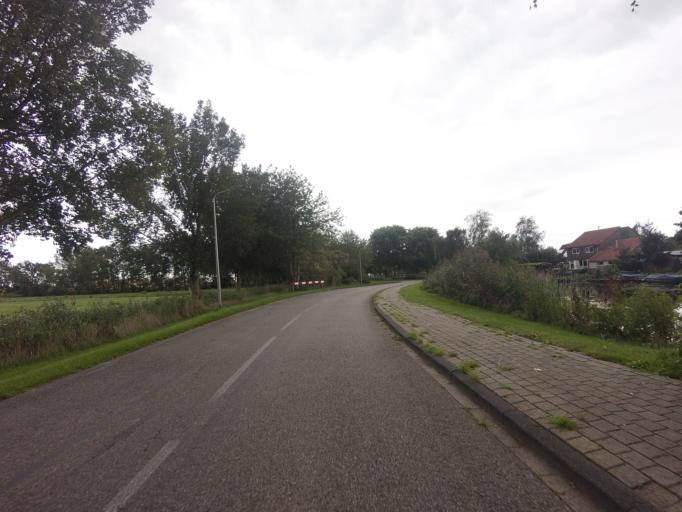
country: NL
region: Friesland
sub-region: Sudwest Fryslan
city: IJlst
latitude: 53.0079
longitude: 5.6338
